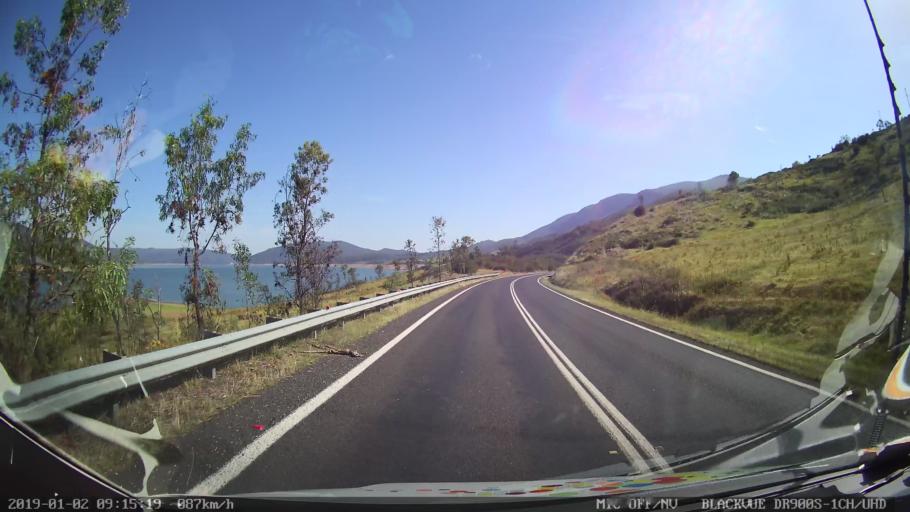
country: AU
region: New South Wales
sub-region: Tumut Shire
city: Tumut
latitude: -35.4663
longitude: 148.2786
